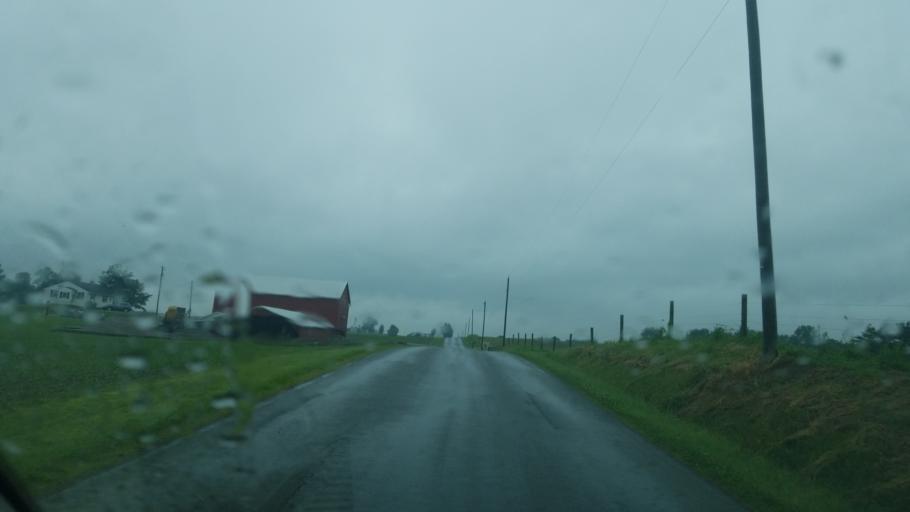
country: US
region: Ohio
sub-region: Huron County
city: Greenwich
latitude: 40.9384
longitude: -82.5696
